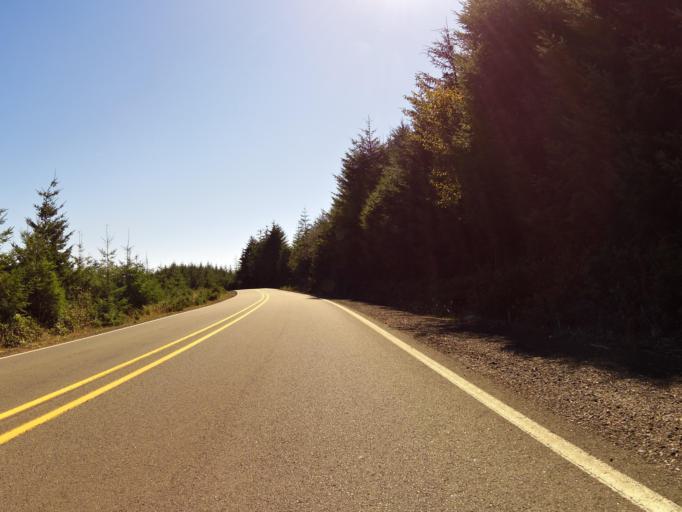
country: US
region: Oregon
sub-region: Coos County
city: Barview
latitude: 43.2516
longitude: -124.3371
